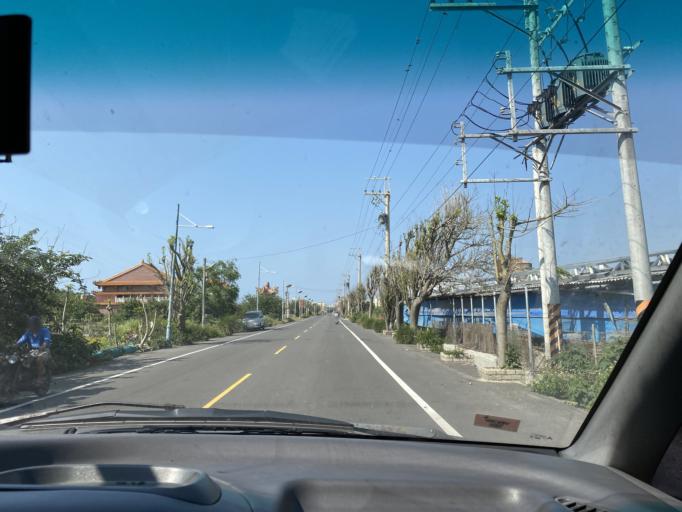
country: TW
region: Taiwan
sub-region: Changhua
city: Chang-hua
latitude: 23.9556
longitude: 120.3350
